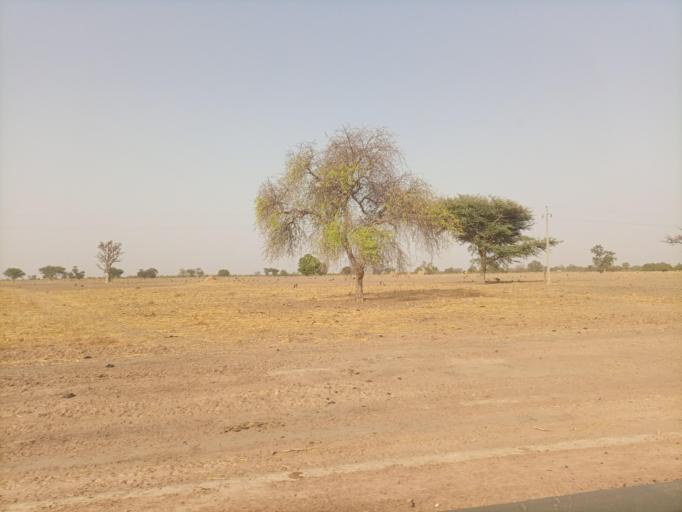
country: SN
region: Fatick
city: Passi
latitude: 14.0267
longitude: -16.3046
